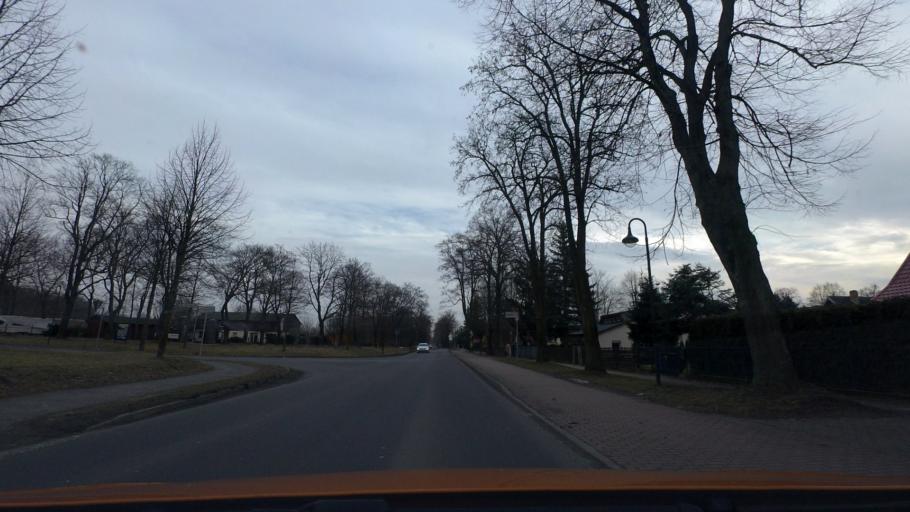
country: DE
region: Brandenburg
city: Ahrensfelde
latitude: 52.5833
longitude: 13.5664
